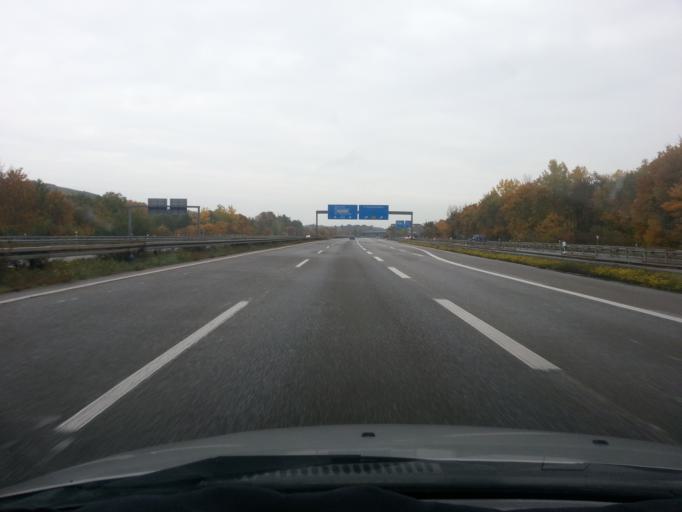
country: DE
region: Hesse
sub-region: Regierungsbezirk Darmstadt
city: Neu Isenburg
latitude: 50.0628
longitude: 8.7262
